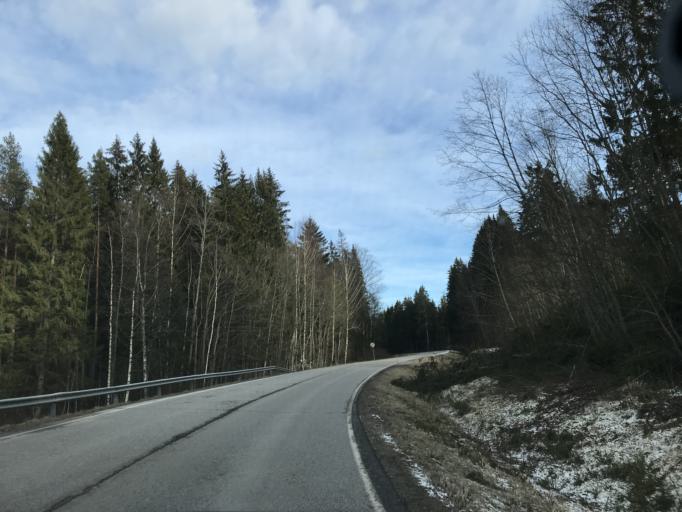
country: FI
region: Uusimaa
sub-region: Raaseporin
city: Pohja
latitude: 60.0903
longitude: 23.4323
